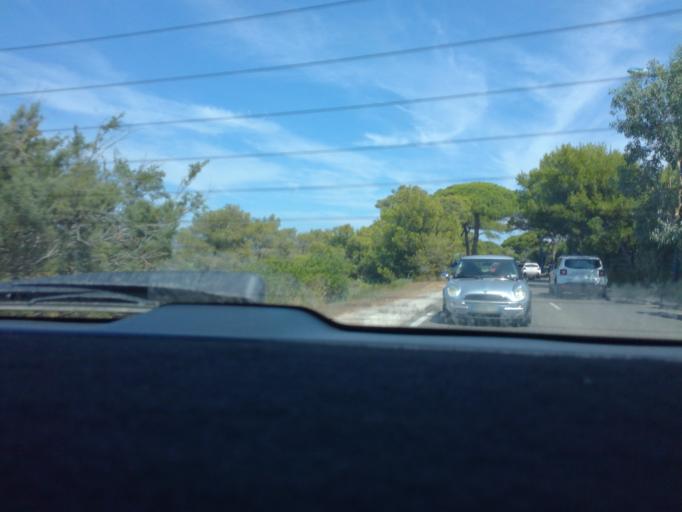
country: FR
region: Provence-Alpes-Cote d'Azur
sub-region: Departement du Var
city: Hyeres
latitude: 43.0516
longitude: 6.1468
